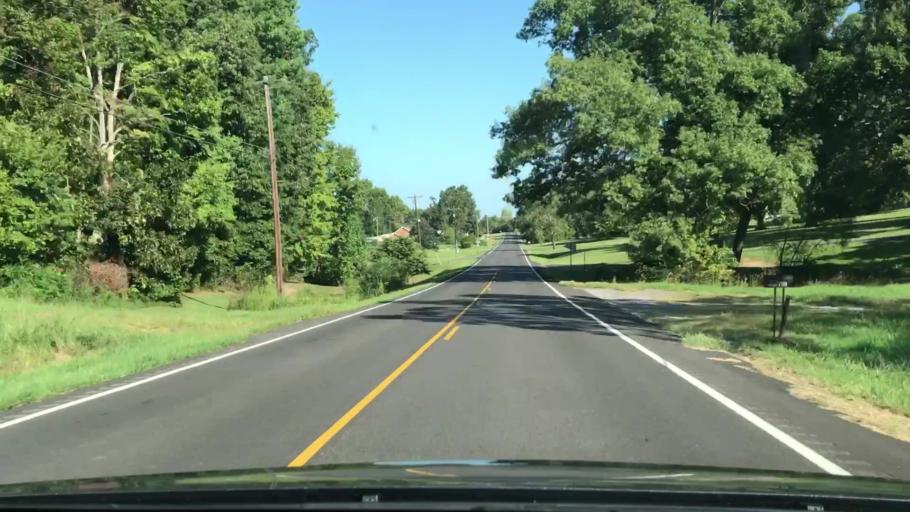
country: US
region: Kentucky
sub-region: Marshall County
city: Benton
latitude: 36.7711
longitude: -88.4401
